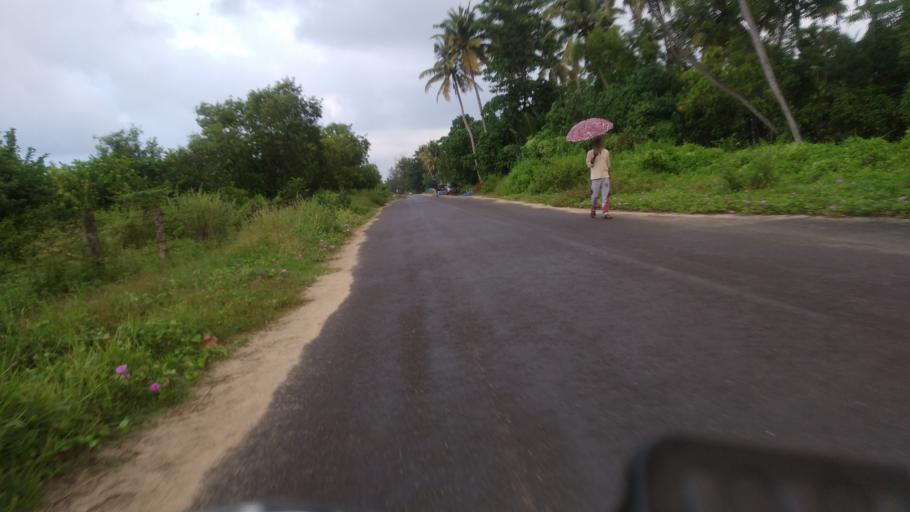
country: IN
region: Kerala
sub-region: Ernakulam
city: Cochin
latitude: 10.0043
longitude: 76.2190
